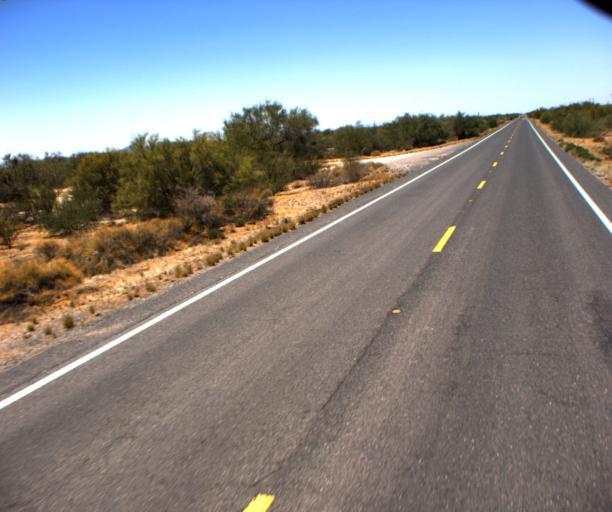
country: US
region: Arizona
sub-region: Pinal County
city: Florence
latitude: 32.8019
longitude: -111.1841
